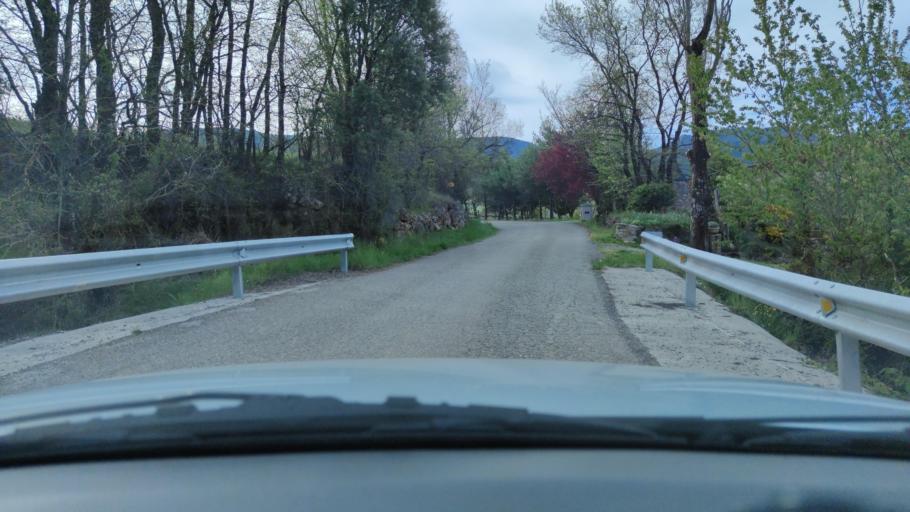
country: ES
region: Catalonia
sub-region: Provincia de Lleida
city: Coll de Nargo
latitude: 42.2344
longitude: 1.3921
